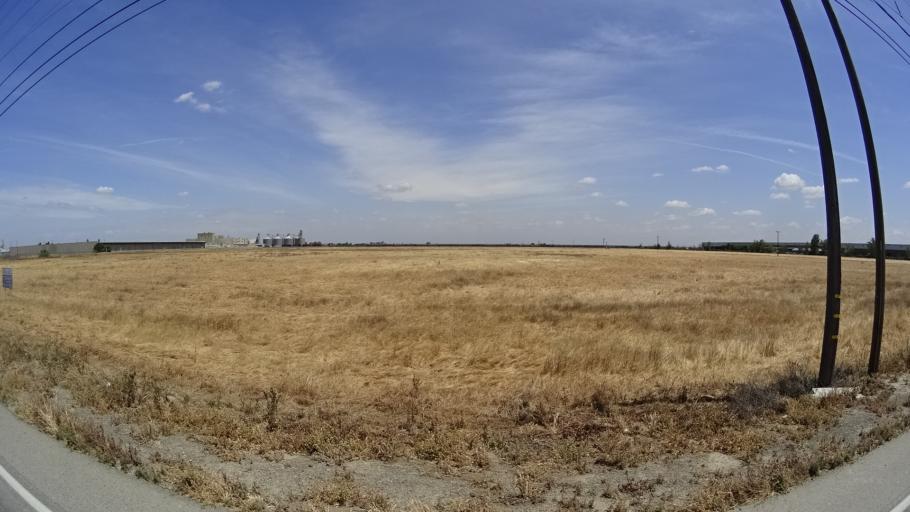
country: US
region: California
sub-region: Kings County
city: Home Garden
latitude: 36.2632
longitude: -119.6549
